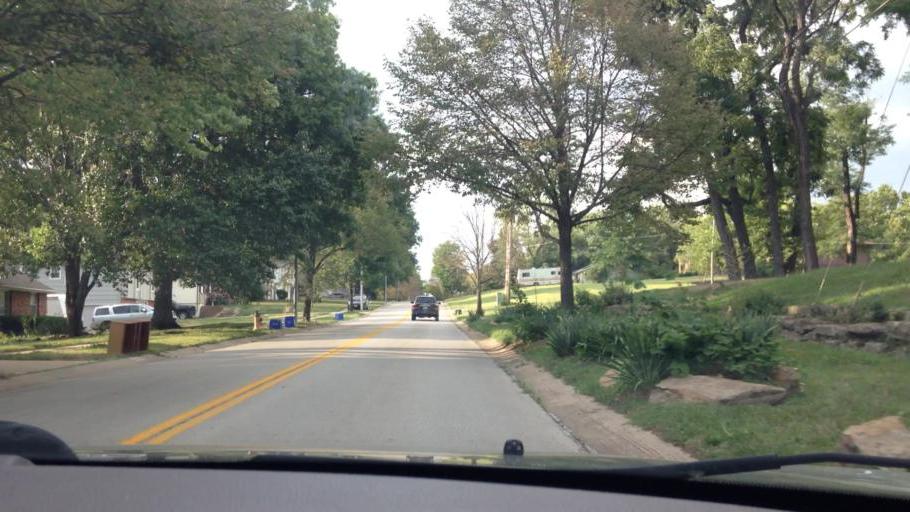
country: US
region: Missouri
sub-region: Platte County
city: Parkville
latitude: 39.2178
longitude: -94.6405
